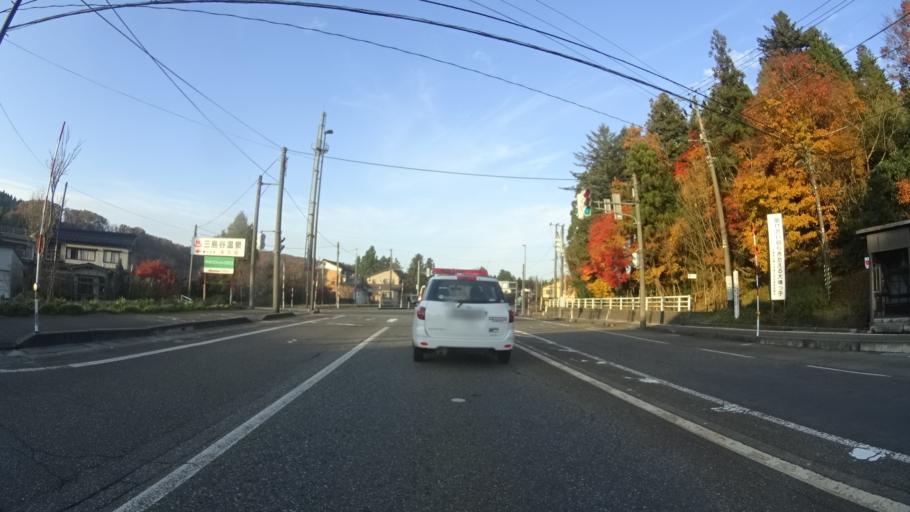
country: JP
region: Niigata
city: Nagaoka
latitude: 37.4334
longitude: 138.7283
